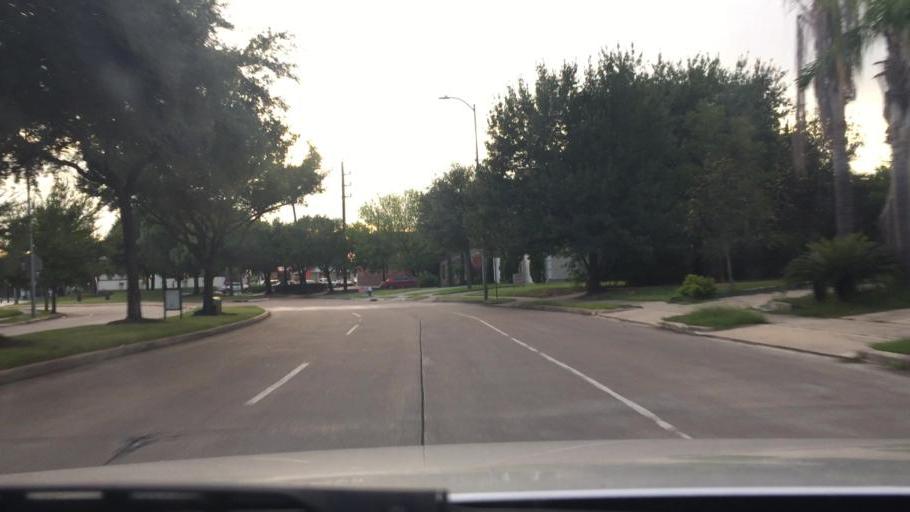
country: US
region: Texas
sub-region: Harris County
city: Bellaire
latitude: 29.7356
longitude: -95.4750
